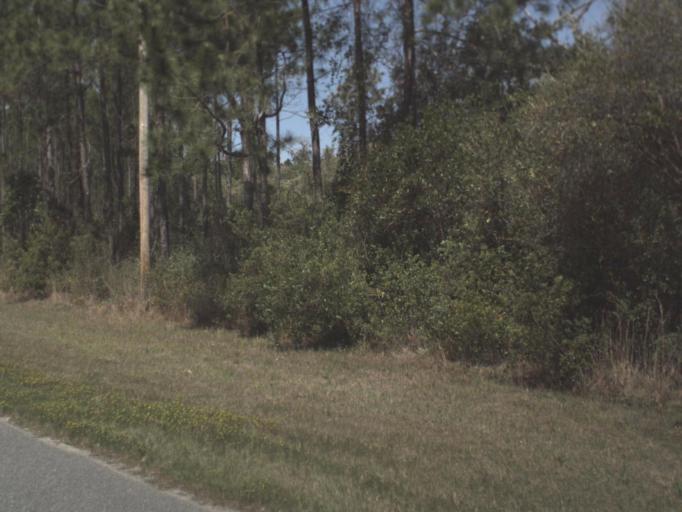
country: US
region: Florida
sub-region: Bay County
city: Lynn Haven
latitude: 30.3279
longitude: -85.7128
